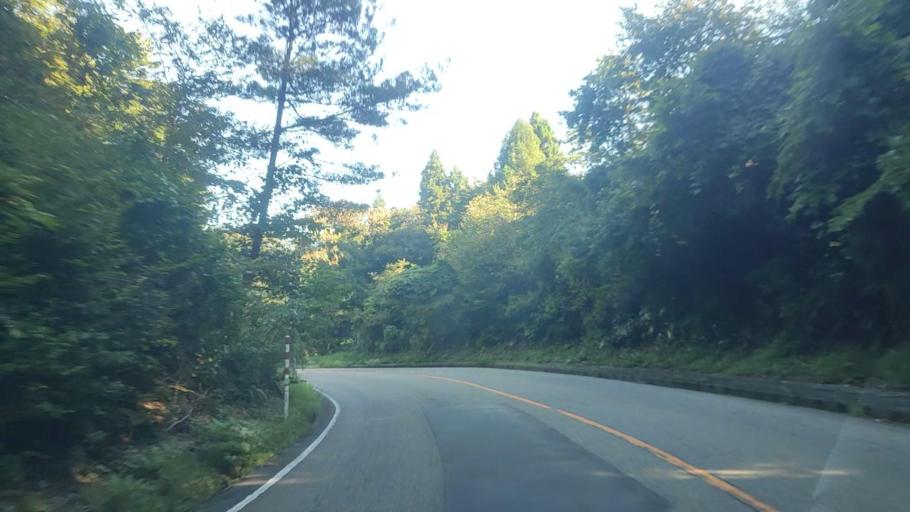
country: JP
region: Ishikawa
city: Nanao
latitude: 37.1009
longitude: 136.9488
